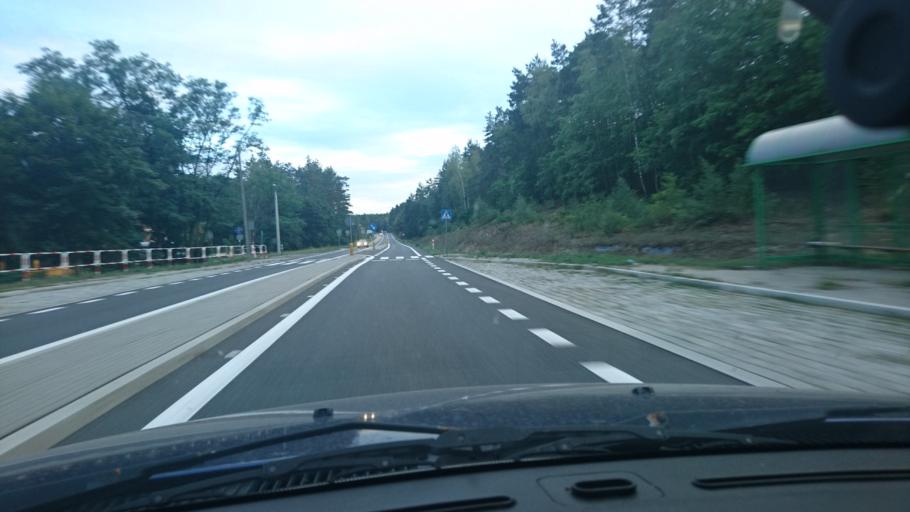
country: PL
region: Silesian Voivodeship
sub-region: Powiat tarnogorski
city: Tworog
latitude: 50.5963
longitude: 18.7023
